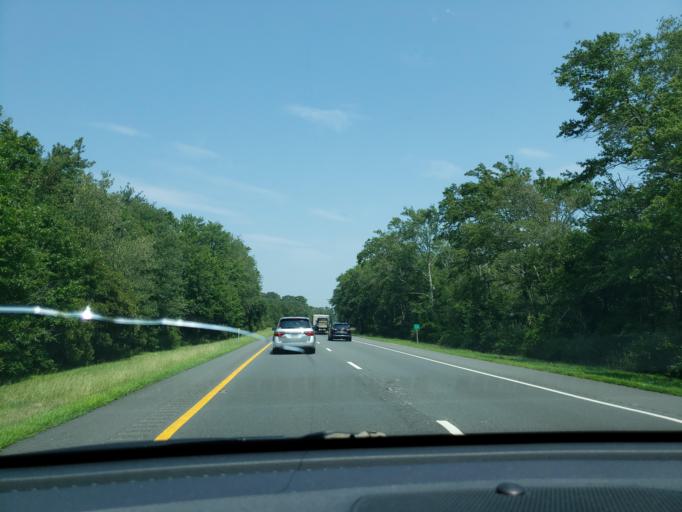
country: US
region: New Jersey
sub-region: Cape May County
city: Avalon
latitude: 39.1435
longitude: -74.7594
